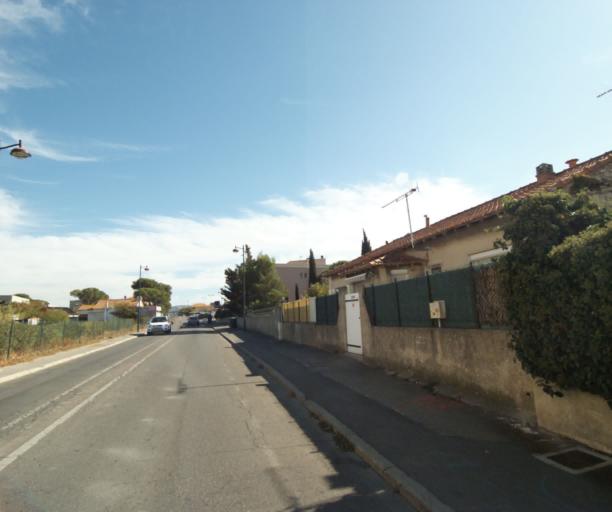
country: FR
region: Provence-Alpes-Cote d'Azur
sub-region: Departement des Bouches-du-Rhone
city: Saint-Victoret
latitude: 43.4187
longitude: 5.2388
